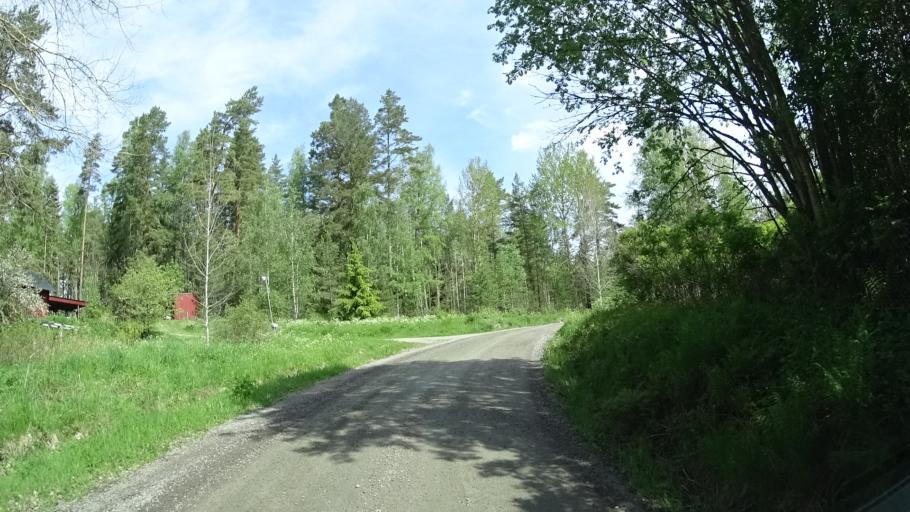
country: SE
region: OEstergoetland
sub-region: Finspangs Kommun
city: Finspang
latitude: 58.7613
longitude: 15.8331
